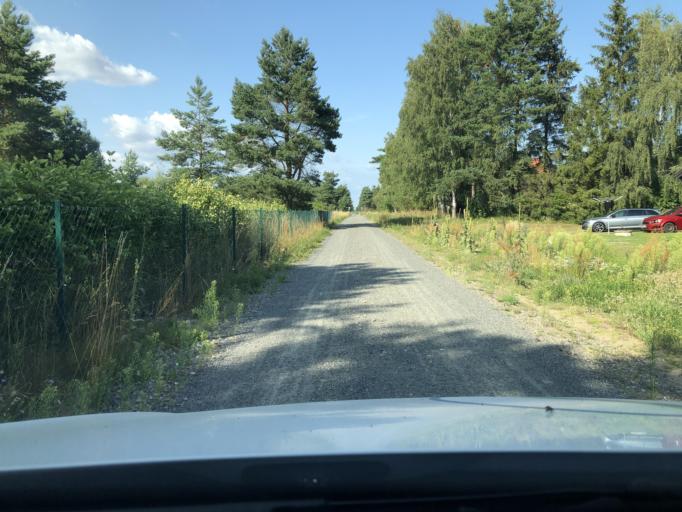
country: SE
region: Skane
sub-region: Kristianstads Kommun
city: Norra Asum
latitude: 55.9315
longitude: 14.1340
